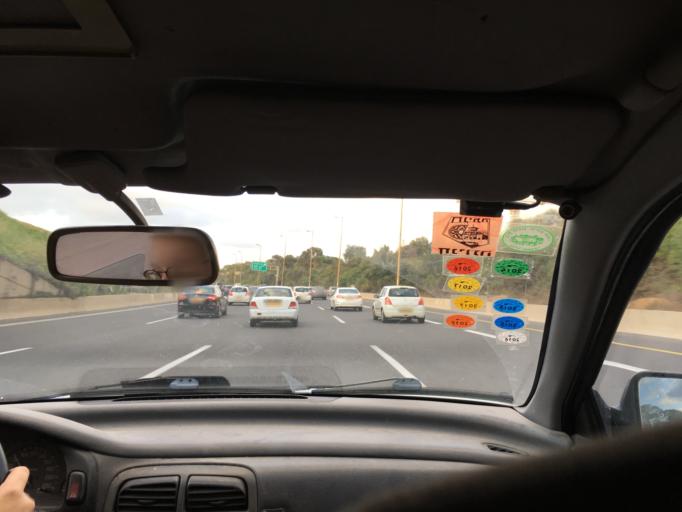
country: IL
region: Tel Aviv
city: Ramat Gan
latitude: 32.1128
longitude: 34.8108
